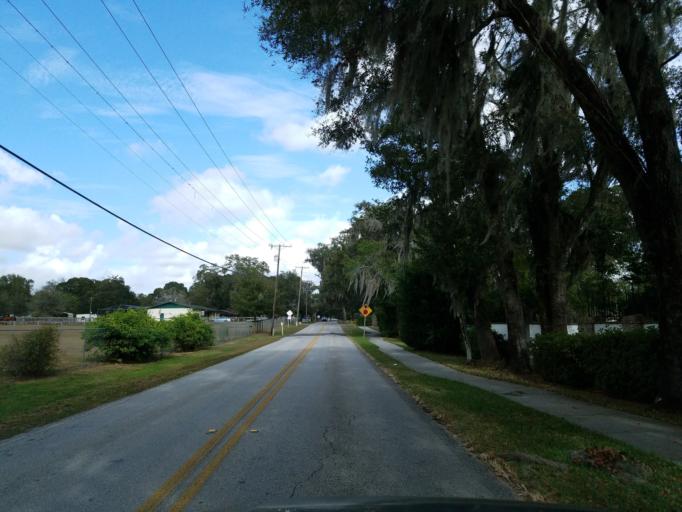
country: US
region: Florida
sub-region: Hillsborough County
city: Bloomingdale
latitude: 27.9060
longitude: -82.2198
